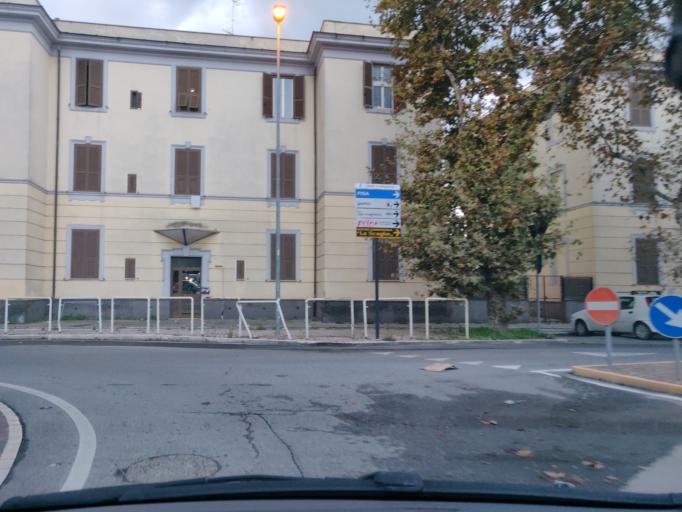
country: IT
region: Latium
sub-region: Citta metropolitana di Roma Capitale
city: Civitavecchia
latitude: 42.0912
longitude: 11.8017
